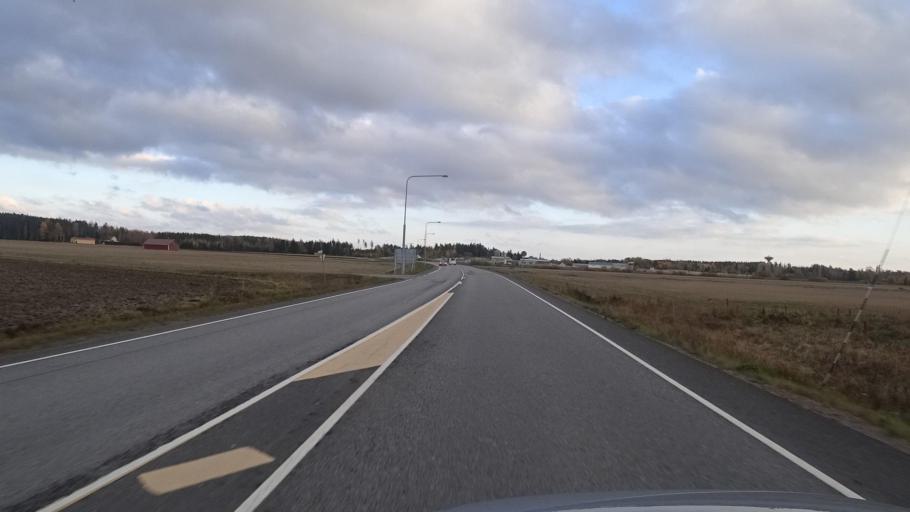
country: FI
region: Varsinais-Suomi
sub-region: Loimaa
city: Loimaa
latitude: 60.8687
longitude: 23.0052
